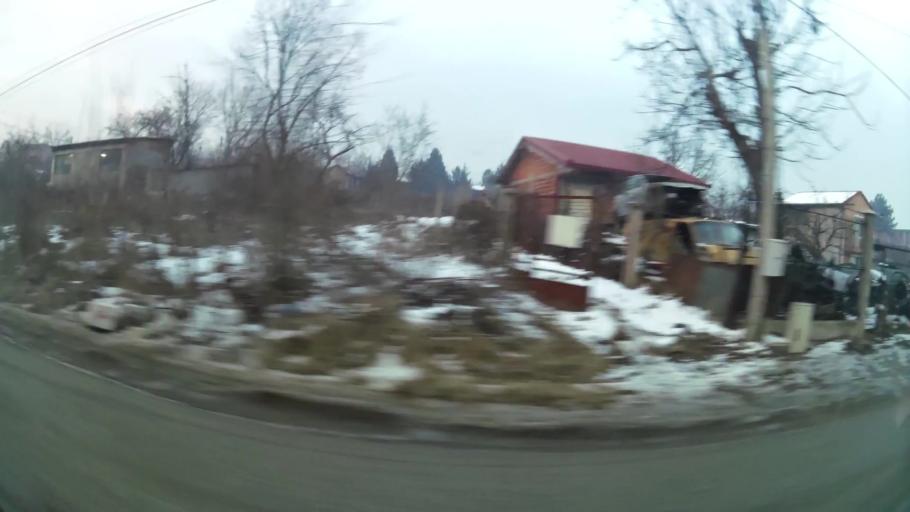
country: MK
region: Suto Orizari
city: Suto Orizare
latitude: 42.0283
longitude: 21.4088
